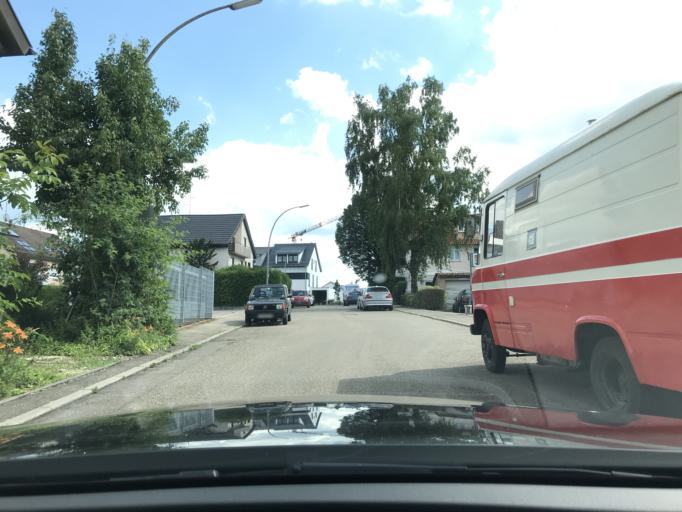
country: DE
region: Baden-Wuerttemberg
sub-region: Regierungsbezirk Stuttgart
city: Waiblingen
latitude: 48.8128
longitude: 9.3207
